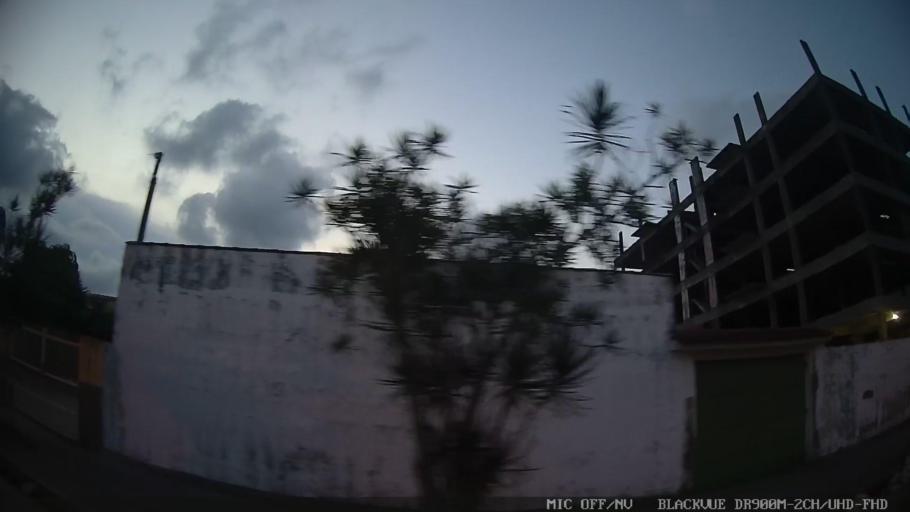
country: BR
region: Sao Paulo
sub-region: Peruibe
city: Peruibe
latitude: -24.3197
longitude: -46.9978
